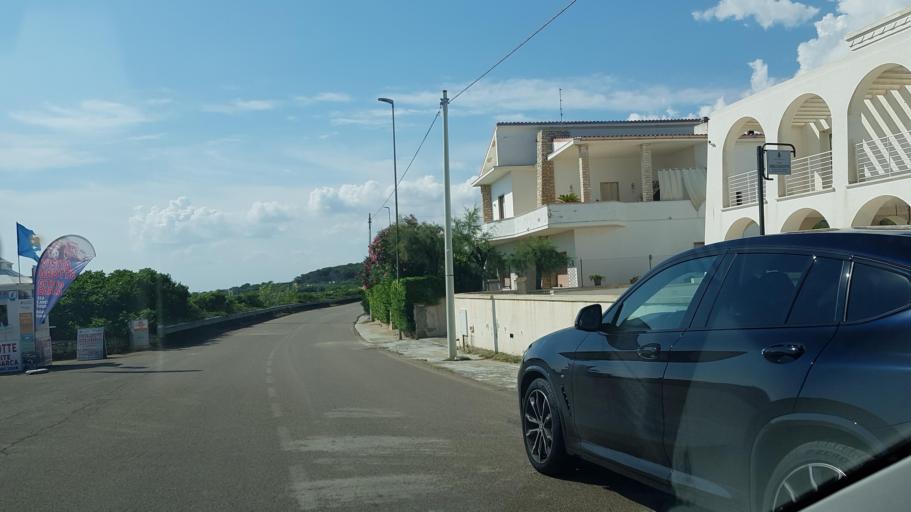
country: IT
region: Apulia
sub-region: Provincia di Lecce
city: Leuca
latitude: 39.7930
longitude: 18.3435
